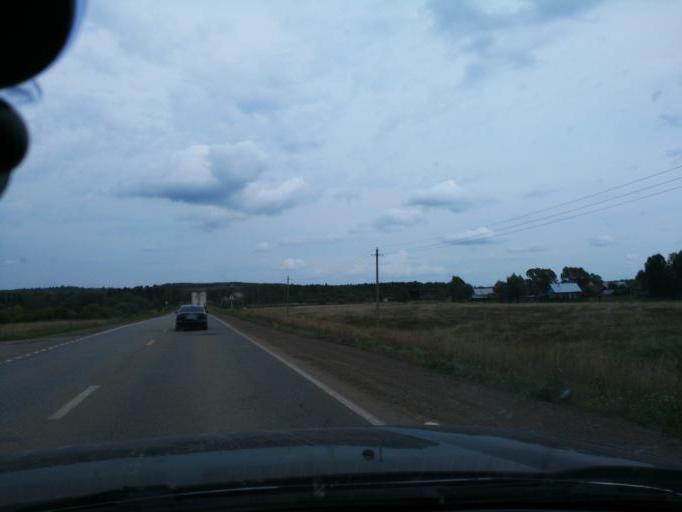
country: RU
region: Perm
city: Kuyeda
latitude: 56.4532
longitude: 55.6137
